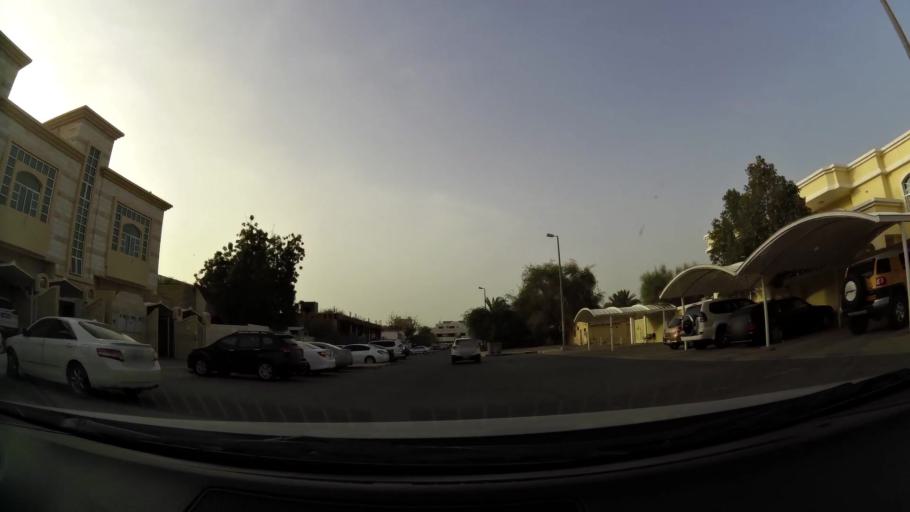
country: AE
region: Abu Dhabi
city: Al Ain
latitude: 24.2435
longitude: 55.7289
